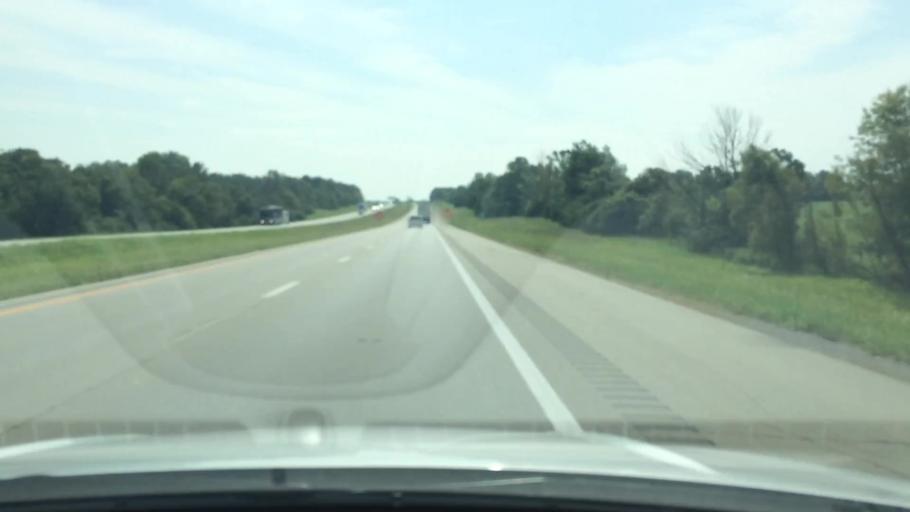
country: US
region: Kentucky
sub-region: Scott County
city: Georgetown
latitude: 38.1267
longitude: -84.5517
